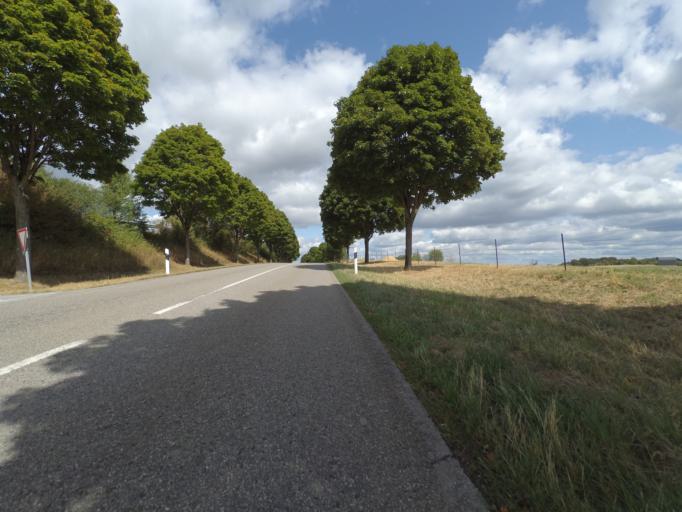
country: LU
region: Grevenmacher
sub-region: Canton de Grevenmacher
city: Flaxweiler
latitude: 49.6571
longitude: 6.3398
